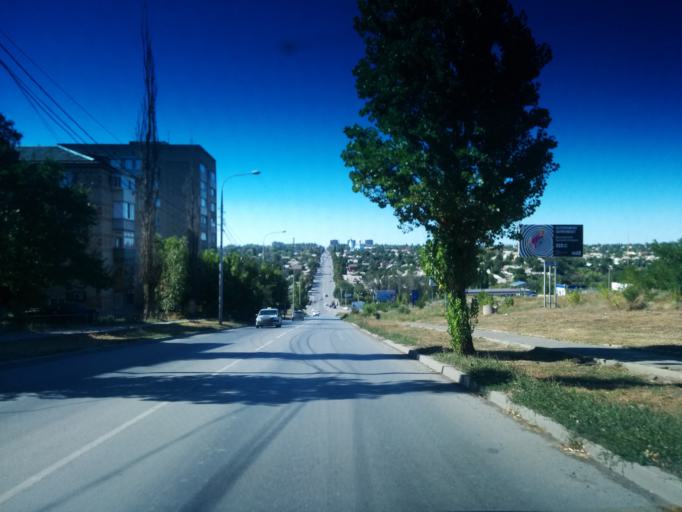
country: RU
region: Rostov
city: Shakhty
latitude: 47.6964
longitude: 40.2413
